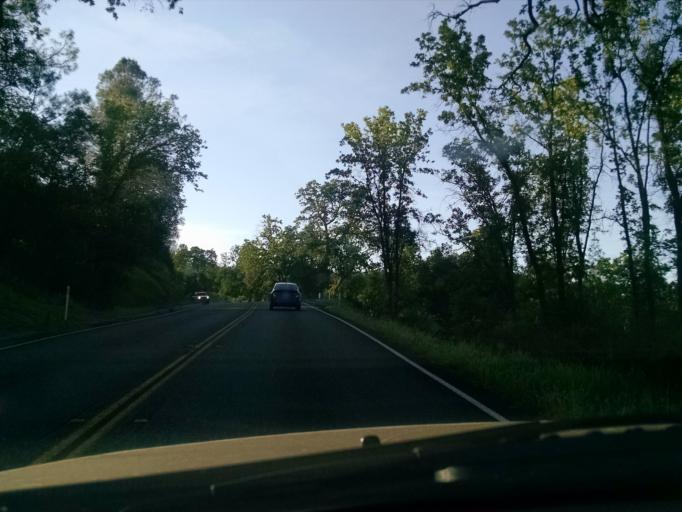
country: US
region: California
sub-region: Madera County
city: Ahwahnee
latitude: 37.3808
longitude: -119.7321
